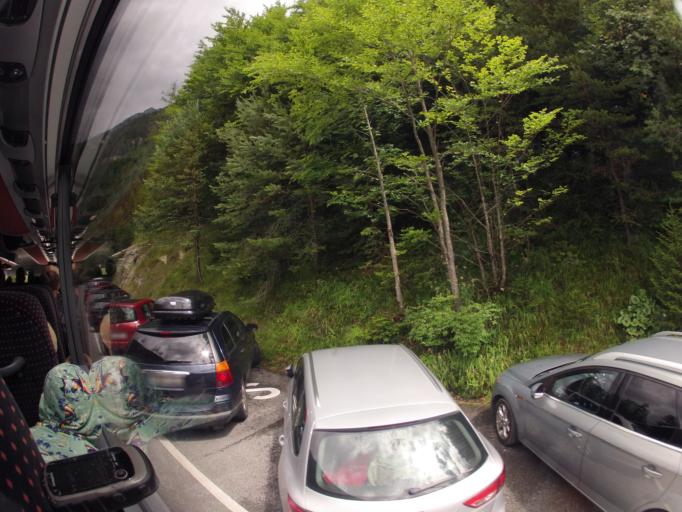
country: AT
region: Salzburg
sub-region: Politischer Bezirk Sankt Johann im Pongau
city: Werfen
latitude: 47.4957
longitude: 13.1959
